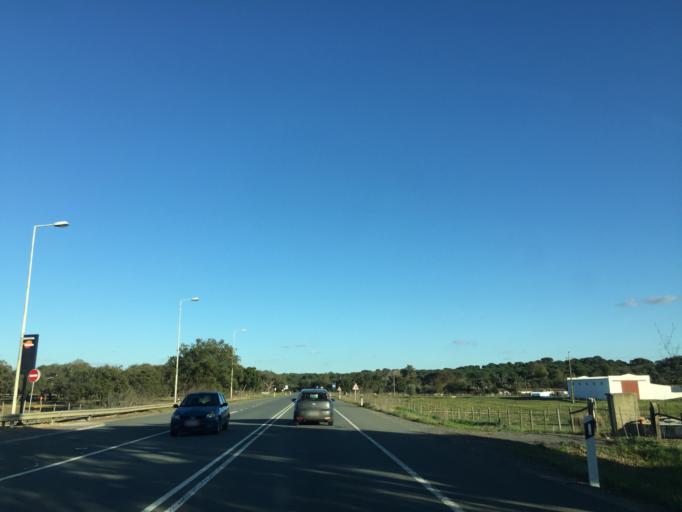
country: PT
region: Setubal
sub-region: Grandola
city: Grandola
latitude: 38.1215
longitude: -8.4454
